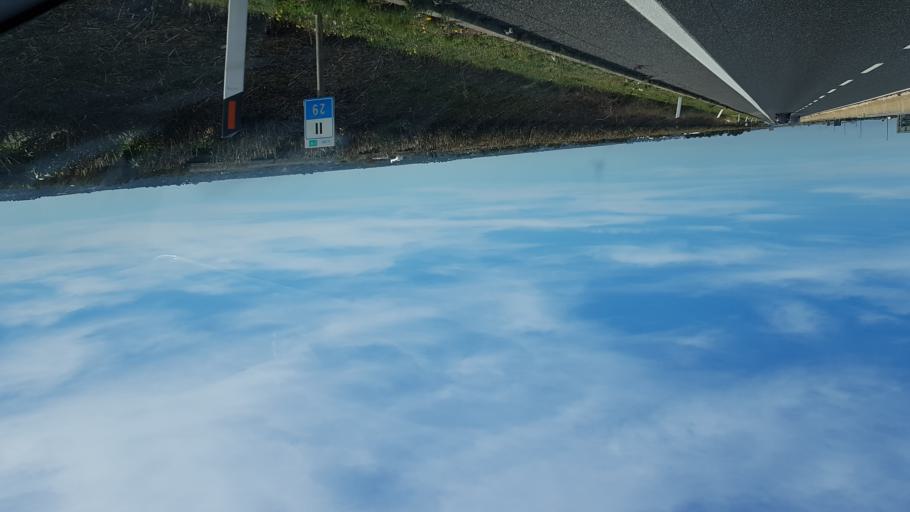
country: IT
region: Apulia
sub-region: Provincia di Brindisi
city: Carovigno
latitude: 40.7484
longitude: 17.7048
